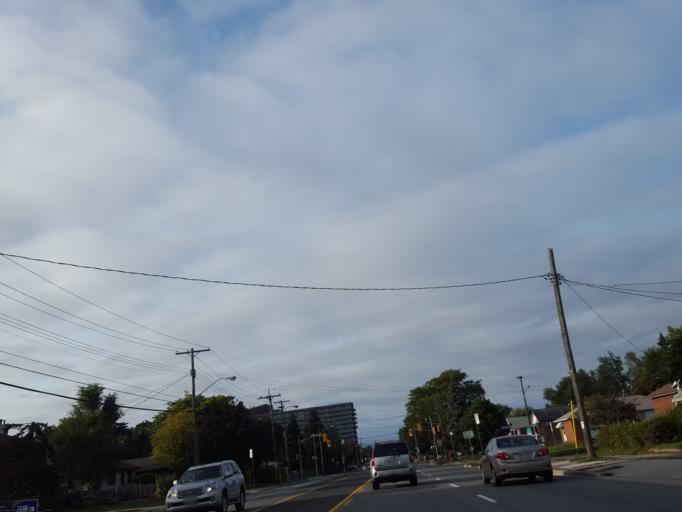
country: CA
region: Ontario
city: Scarborough
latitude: 43.7413
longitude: -79.2931
